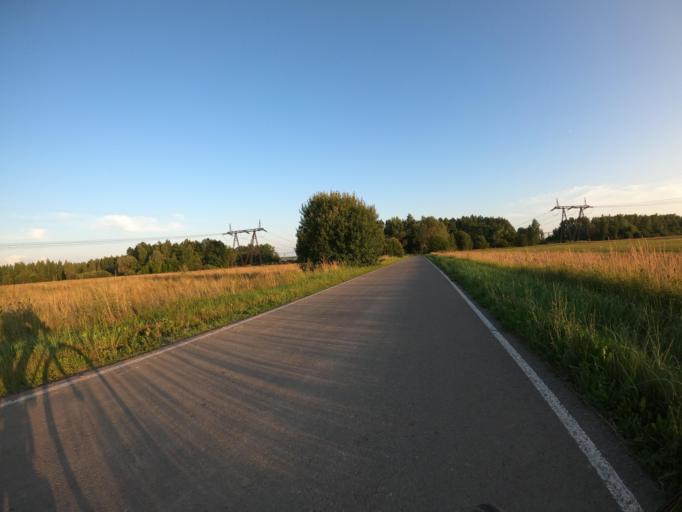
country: RU
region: Moskovskaya
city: Malino
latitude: 55.0963
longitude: 38.2859
